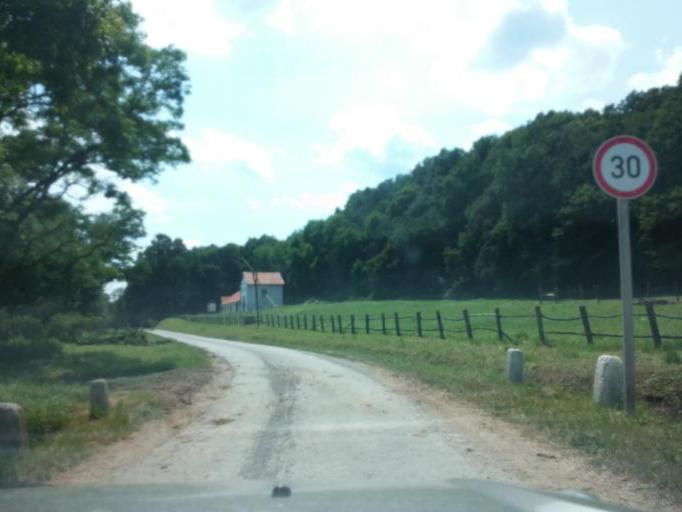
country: HU
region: Somogy
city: Kaposvar
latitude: 46.2535
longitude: 17.7800
